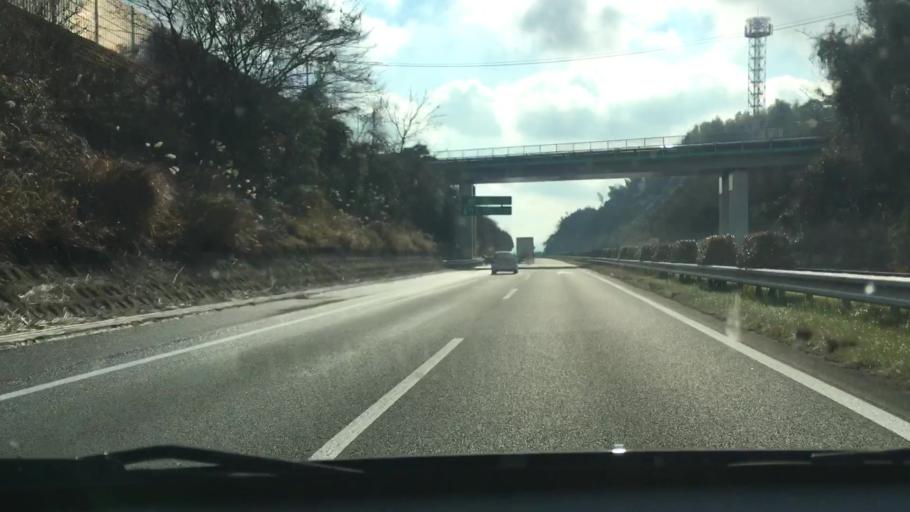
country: JP
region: Kumamoto
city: Kumamoto
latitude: 32.7283
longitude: 130.7737
